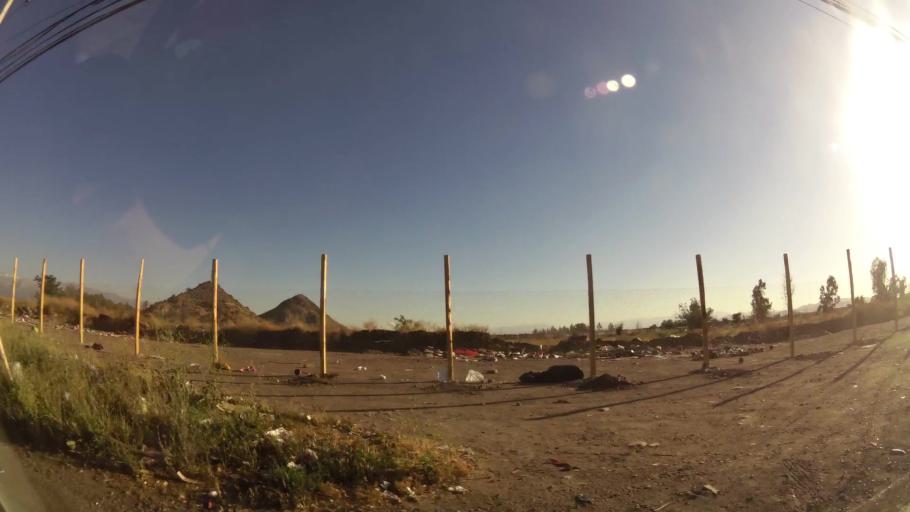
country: CL
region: Santiago Metropolitan
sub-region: Provincia de Maipo
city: San Bernardo
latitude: -33.6057
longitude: -70.6791
